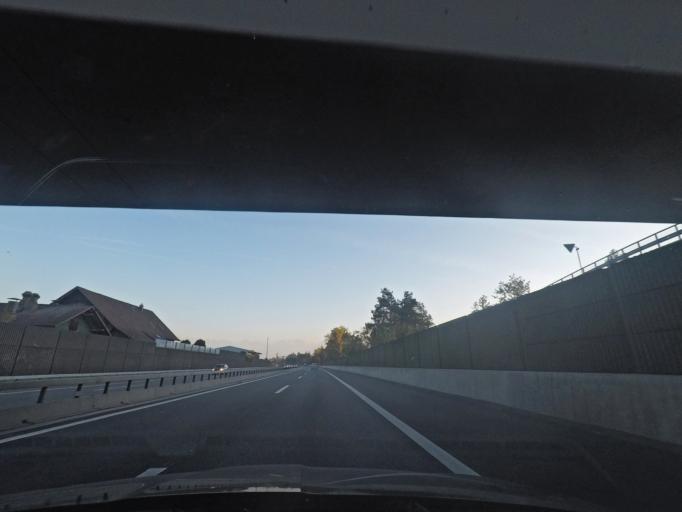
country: CH
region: Bern
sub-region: Bern-Mittelland District
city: Niederwichtrach
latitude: 46.8351
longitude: 7.5617
